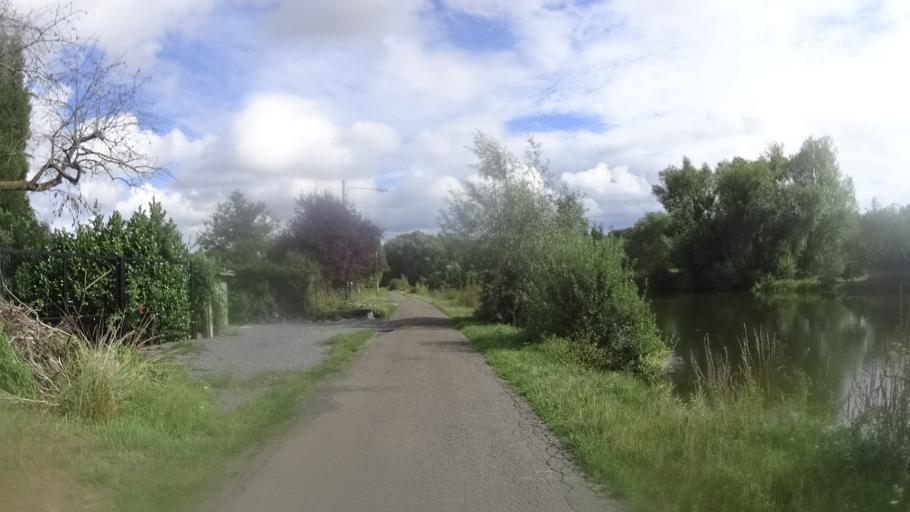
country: BE
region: Wallonia
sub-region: Province du Hainaut
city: Merbes-le-Chateau
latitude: 50.3151
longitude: 4.1841
